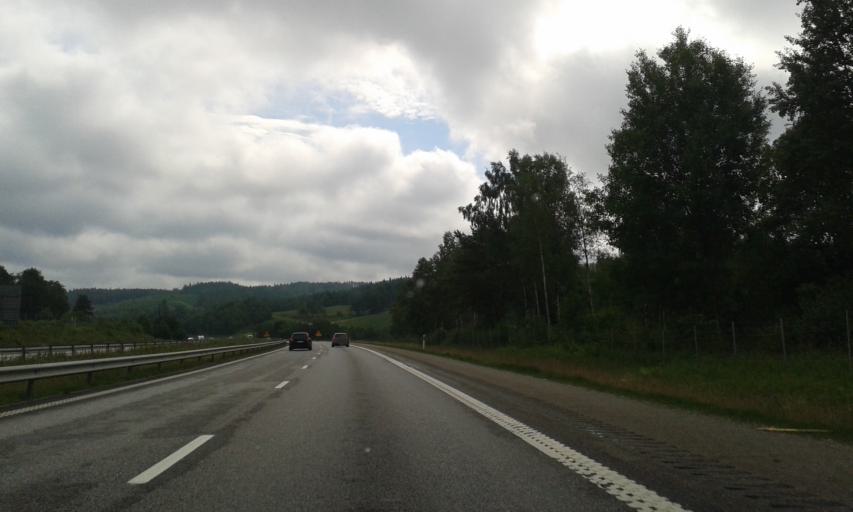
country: SE
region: Vaestra Goetaland
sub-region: Bollebygds Kommun
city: Bollebygd
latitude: 57.6615
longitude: 12.5541
